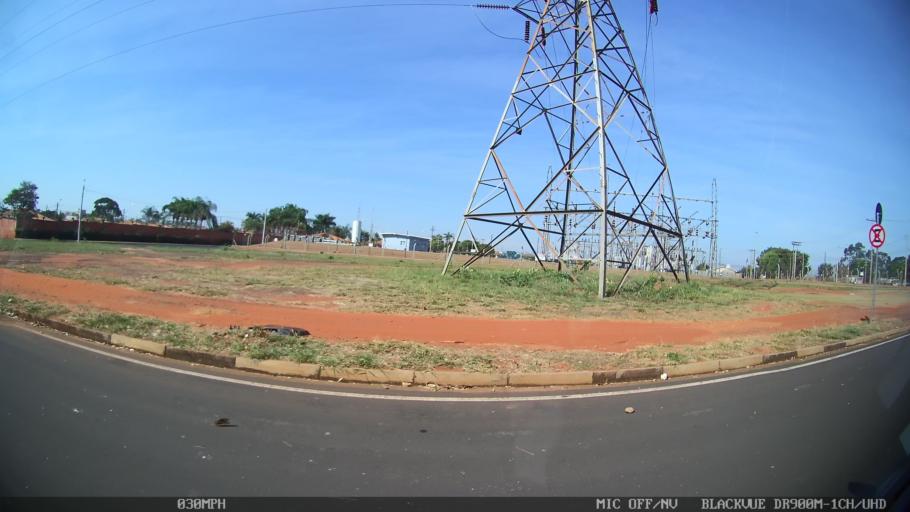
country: BR
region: Sao Paulo
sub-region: Sao Jose Do Rio Preto
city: Sao Jose do Rio Preto
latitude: -20.7881
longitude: -49.3816
